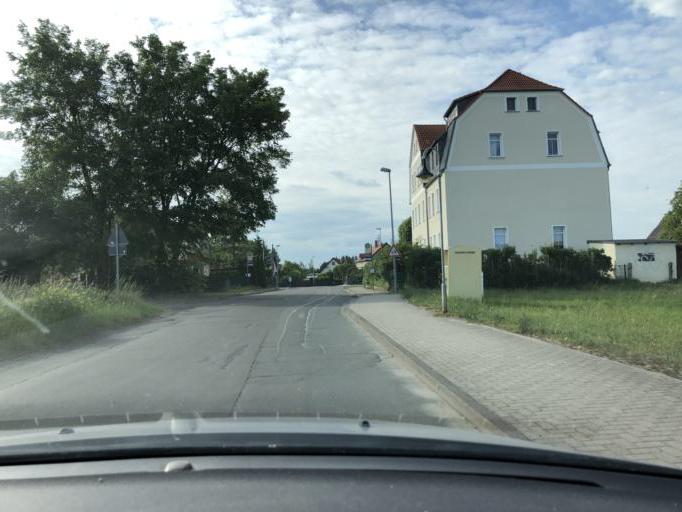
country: DE
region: Saxony
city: Borsdorf
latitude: 51.3394
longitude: 12.5233
